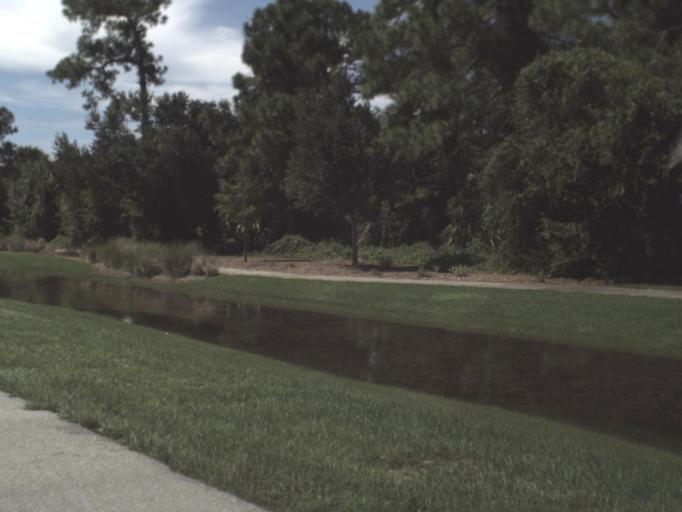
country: US
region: Florida
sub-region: Sarasota County
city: North Port
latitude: 27.0385
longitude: -82.1633
